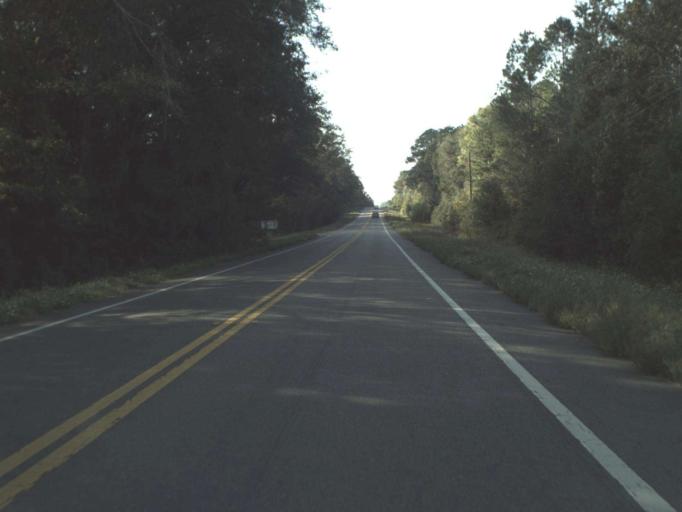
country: US
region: Florida
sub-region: Bay County
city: Laguna Beach
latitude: 30.4453
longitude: -85.8812
